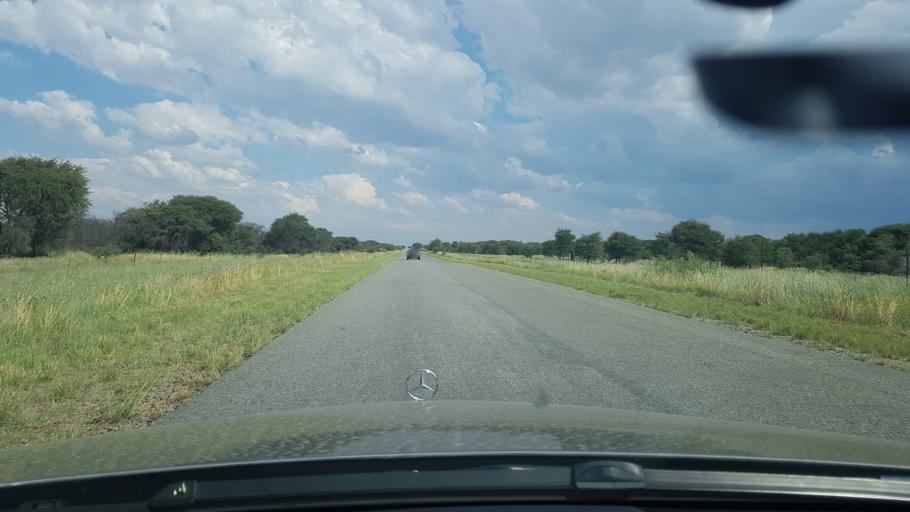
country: ZA
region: North-West
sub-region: Dr Ruth Segomotsi Mompati District Municipality
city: Bloemhof
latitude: -27.7788
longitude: 25.6079
